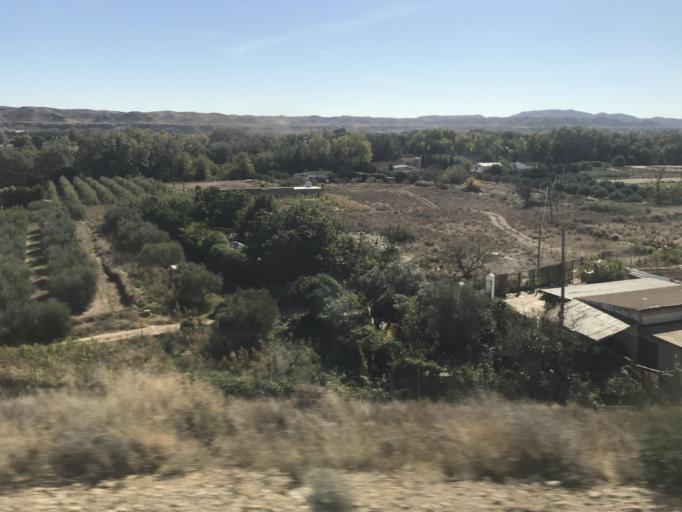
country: ES
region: Aragon
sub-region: Provincia de Zaragoza
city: Plasencia de Jalon
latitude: 41.6911
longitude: -1.2329
